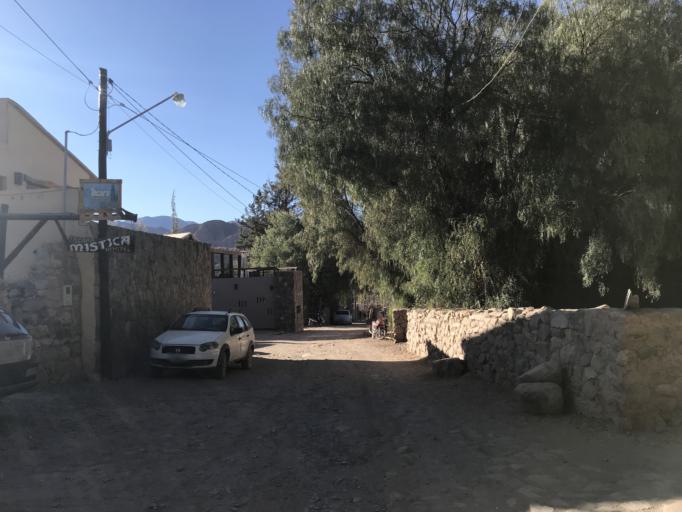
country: AR
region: Jujuy
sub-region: Departamento de Tilcara
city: Tilcara
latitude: -23.5784
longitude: -65.3960
